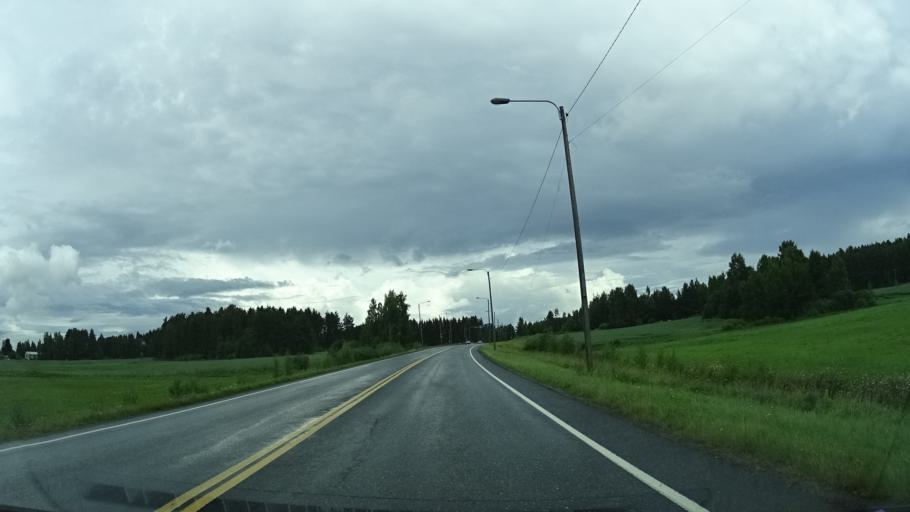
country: FI
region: Pirkanmaa
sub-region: Etelae-Pirkanmaa
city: Valkeakoski
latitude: 61.1663
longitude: 24.0381
